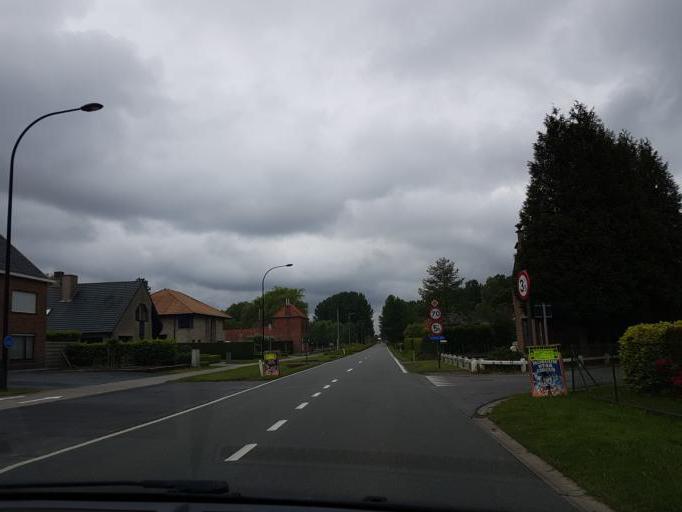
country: BE
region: Flanders
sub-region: Provincie Oost-Vlaanderen
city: Knesselare
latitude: 51.1378
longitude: 3.4078
